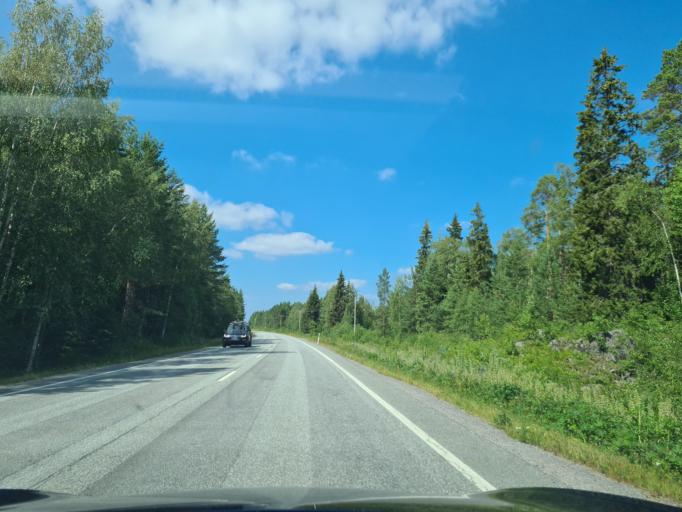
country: FI
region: Ostrobothnia
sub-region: Vaasa
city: Vaasa
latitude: 63.1780
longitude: 21.5757
